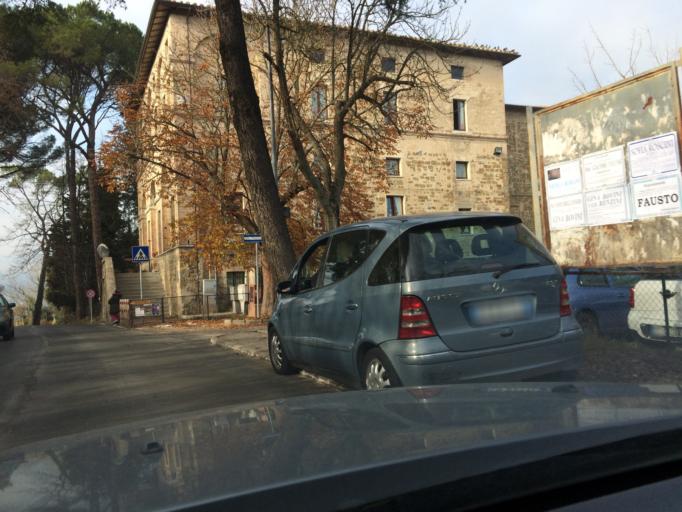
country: IT
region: Umbria
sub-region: Provincia di Perugia
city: Via Lippia
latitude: 43.0866
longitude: 12.4739
